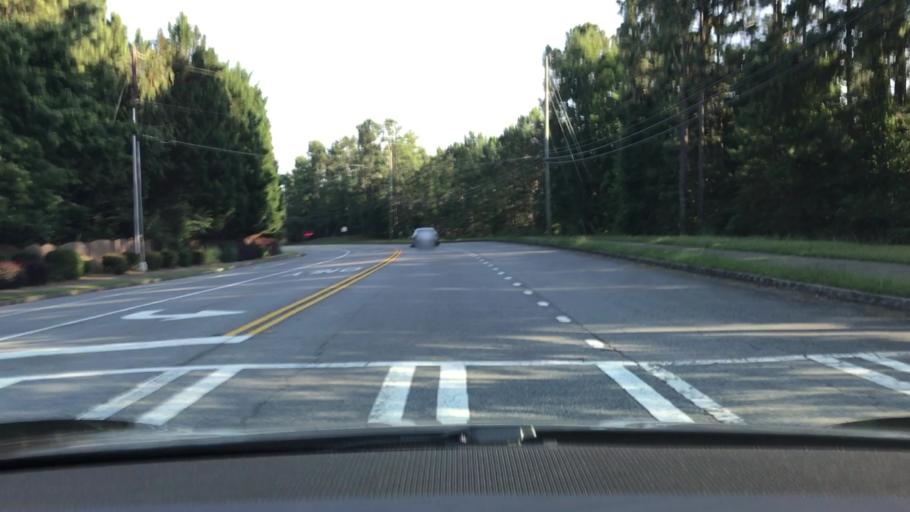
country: US
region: Georgia
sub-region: Fulton County
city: Johns Creek
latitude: 34.0688
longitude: -84.2302
